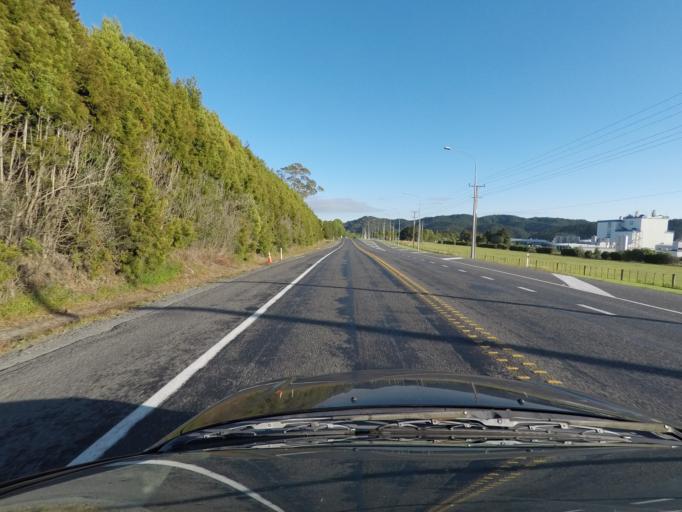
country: NZ
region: Northland
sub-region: Whangarei
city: Whangarei
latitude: -35.6378
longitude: 174.2966
